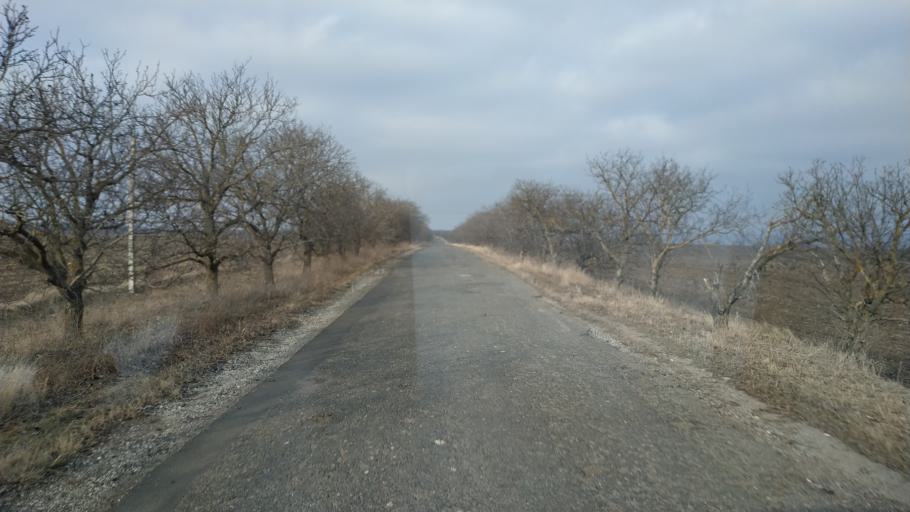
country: MD
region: Hincesti
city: Dancu
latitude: 46.8790
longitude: 28.2977
